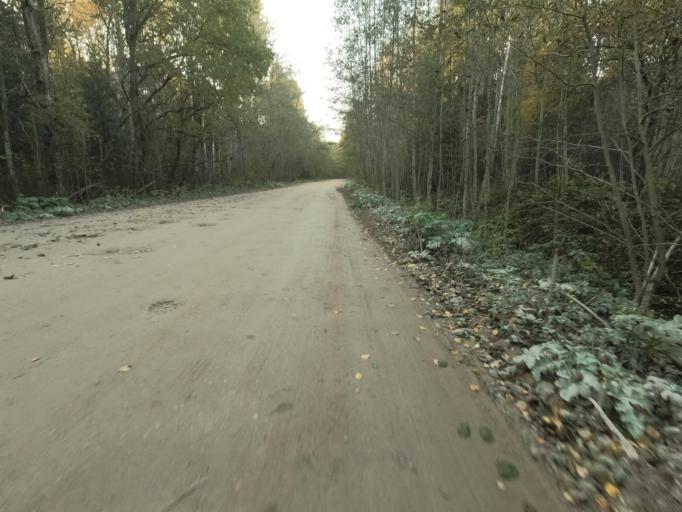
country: RU
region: Leningrad
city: Lyuban'
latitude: 59.0055
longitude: 31.0947
